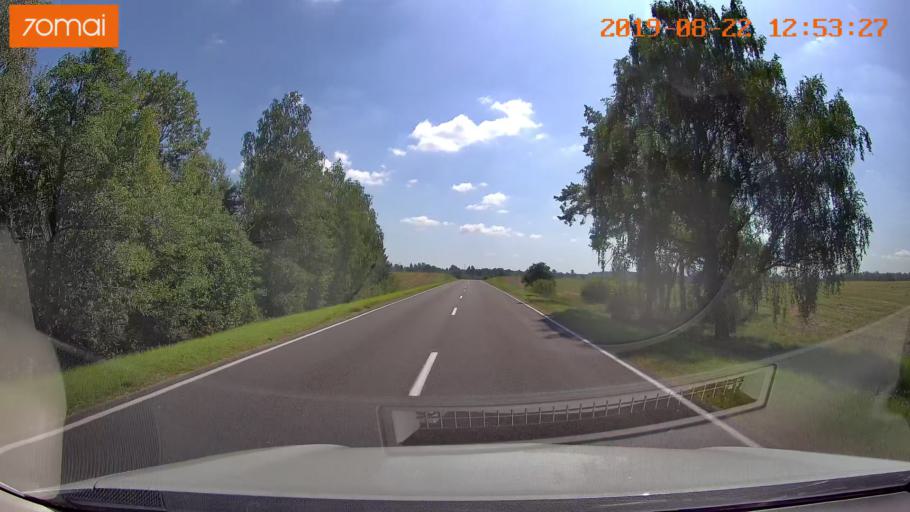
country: BY
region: Minsk
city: Prawdzinski
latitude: 53.4462
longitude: 27.6866
